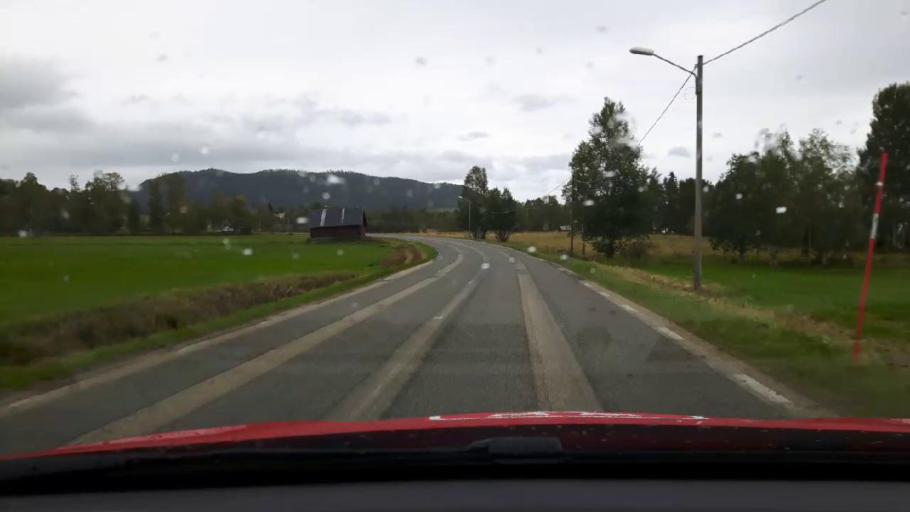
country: SE
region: Jaemtland
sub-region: Bergs Kommun
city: Hoverberg
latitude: 62.7966
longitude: 14.4388
